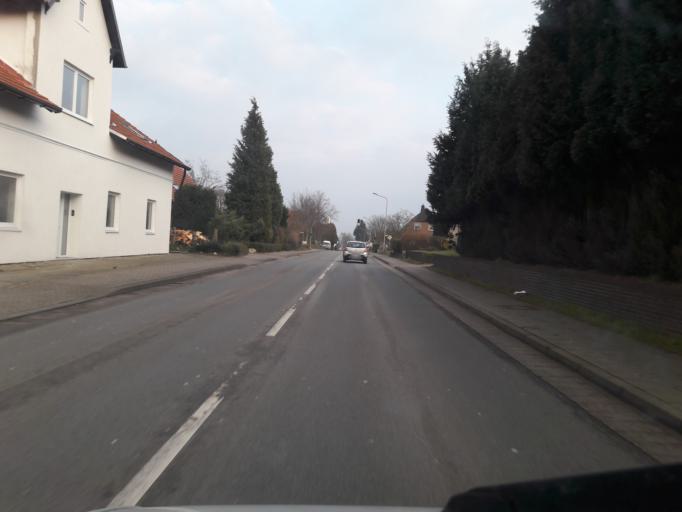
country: DE
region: North Rhine-Westphalia
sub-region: Regierungsbezirk Detmold
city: Hille
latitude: 52.2853
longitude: 8.7494
